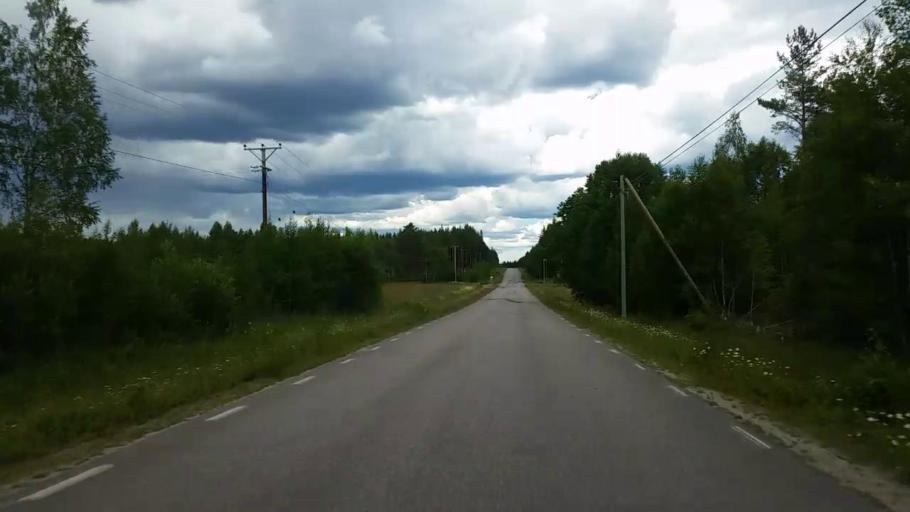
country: SE
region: Gaevleborg
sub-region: Ovanakers Kommun
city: Edsbyn
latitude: 61.4234
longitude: 15.8997
